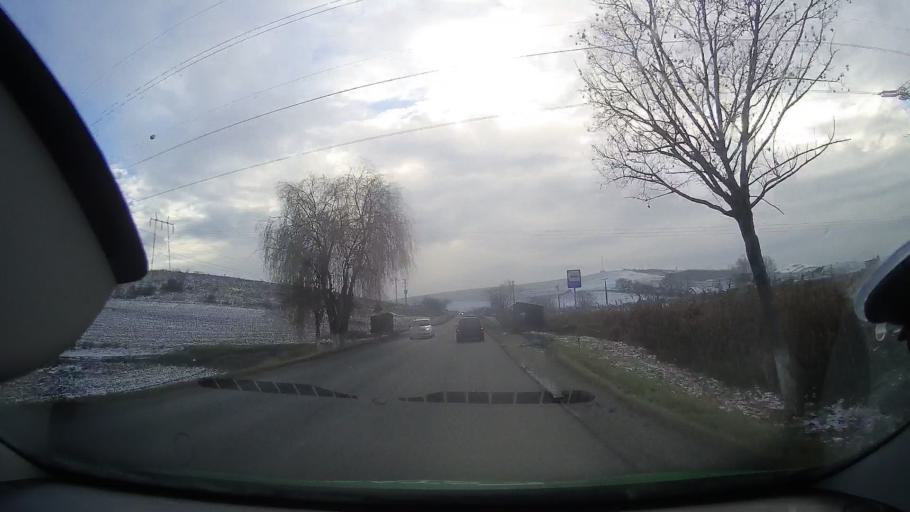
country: RO
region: Mures
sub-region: Comuna Cucerdea
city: Cucerdea
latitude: 46.4216
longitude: 24.2593
